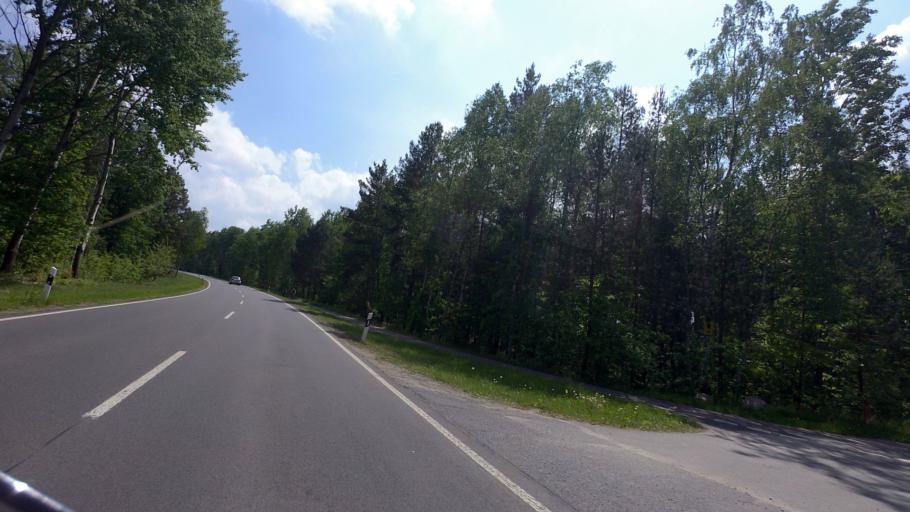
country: DE
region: Saxony
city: Trebendorf
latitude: 51.5290
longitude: 14.5998
